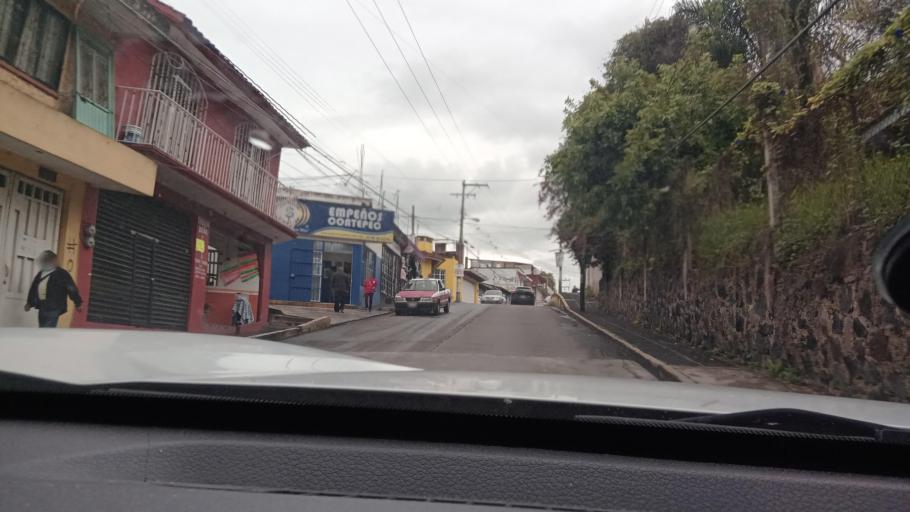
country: MX
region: Veracruz
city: Coatepec
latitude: 19.4497
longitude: -96.9641
